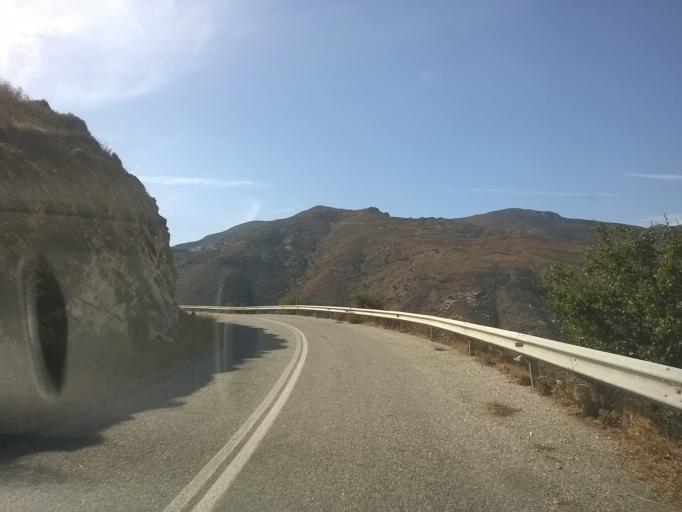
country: GR
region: South Aegean
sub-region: Nomos Kykladon
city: Filotion
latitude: 37.1517
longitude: 25.5507
